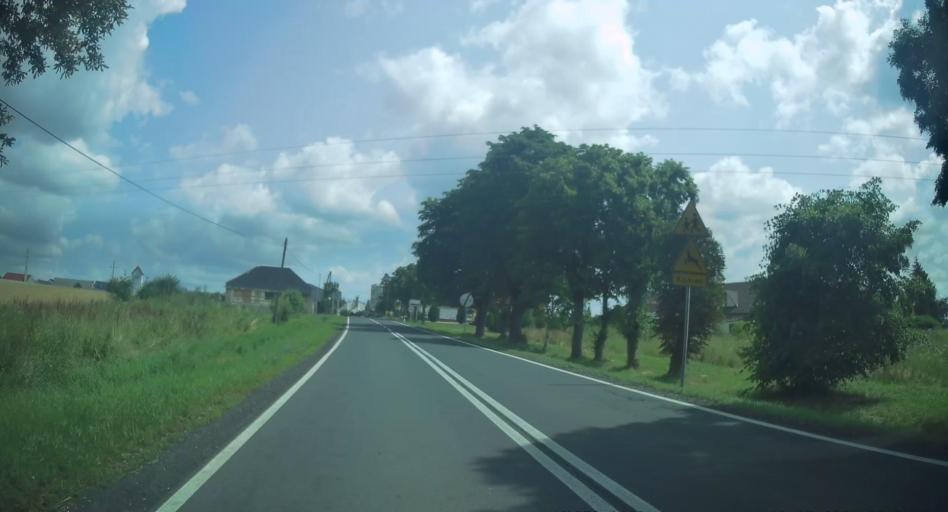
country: PL
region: Opole Voivodeship
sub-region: Powiat prudnicki
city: Twardawa
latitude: 50.3407
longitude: 17.9882
